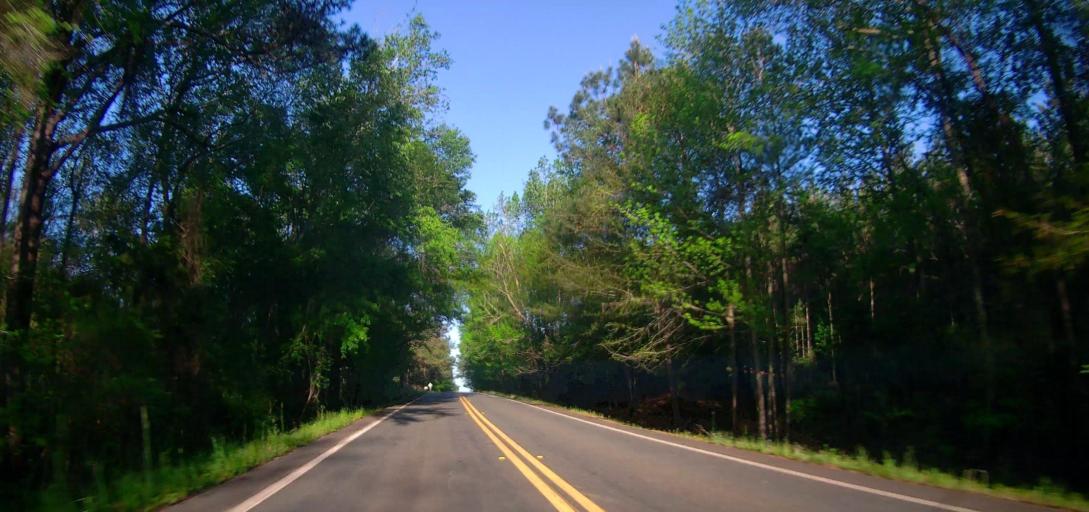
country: US
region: Georgia
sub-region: Schley County
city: Ellaville
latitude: 32.3222
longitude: -84.2379
